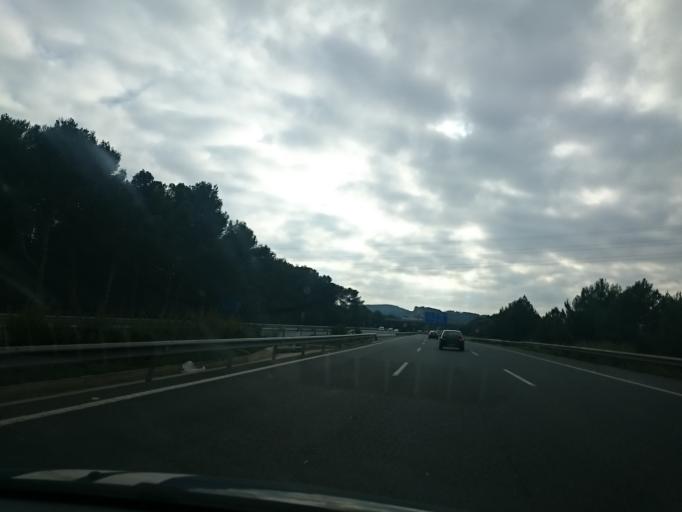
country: ES
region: Catalonia
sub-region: Provincia de Barcelona
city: Sant Pere de Ribes
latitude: 41.2497
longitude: 1.7827
